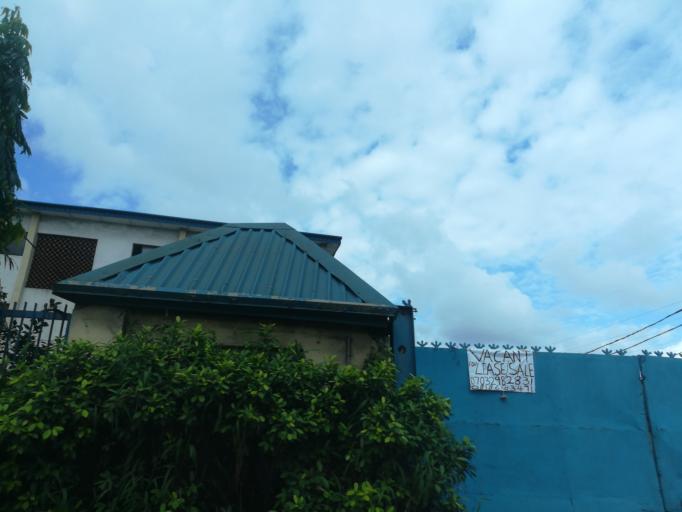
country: NG
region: Lagos
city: Agege
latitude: 6.6178
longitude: 3.3368
